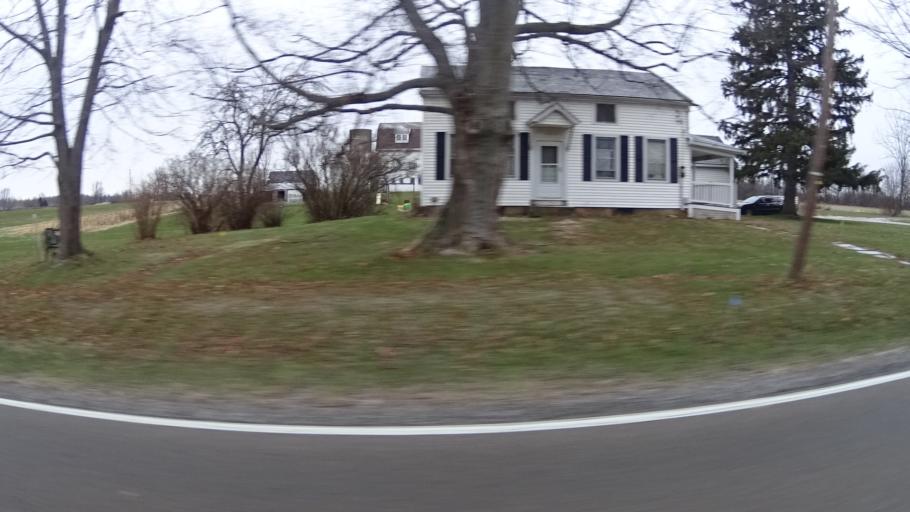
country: US
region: Ohio
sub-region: Lorain County
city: Grafton
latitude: 41.2602
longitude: -82.0170
